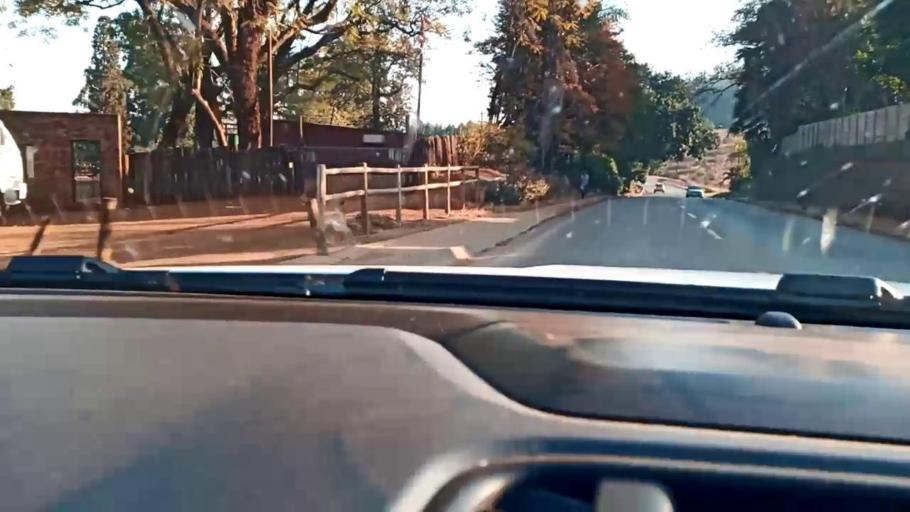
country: ZA
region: Limpopo
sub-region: Mopani District Municipality
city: Duiwelskloof
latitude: -23.6981
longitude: 30.1379
